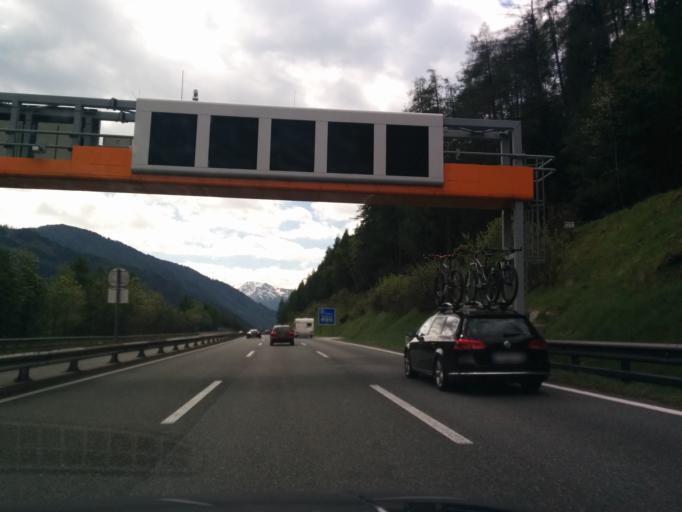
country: AT
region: Tyrol
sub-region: Politischer Bezirk Innsbruck Land
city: Steinach am Brenner
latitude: 47.1030
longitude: 11.4576
